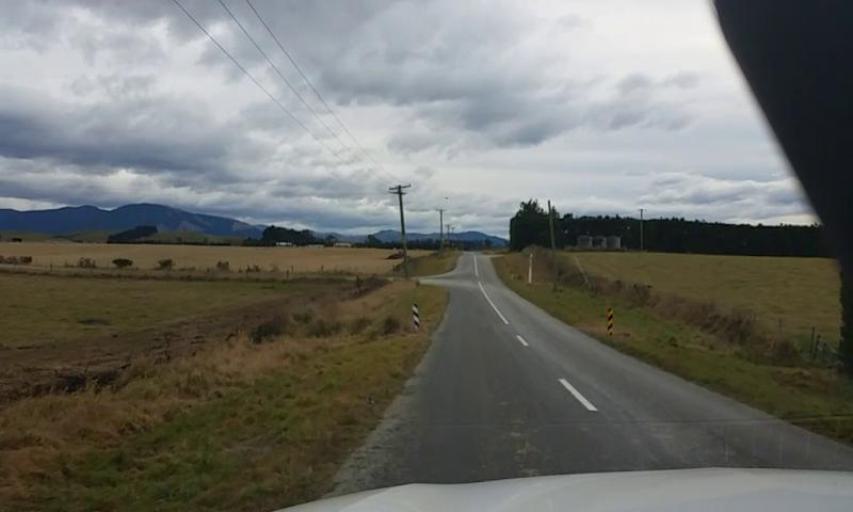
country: NZ
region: Canterbury
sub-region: Waimakariri District
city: Kaiapoi
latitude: -43.2924
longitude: 172.4374
